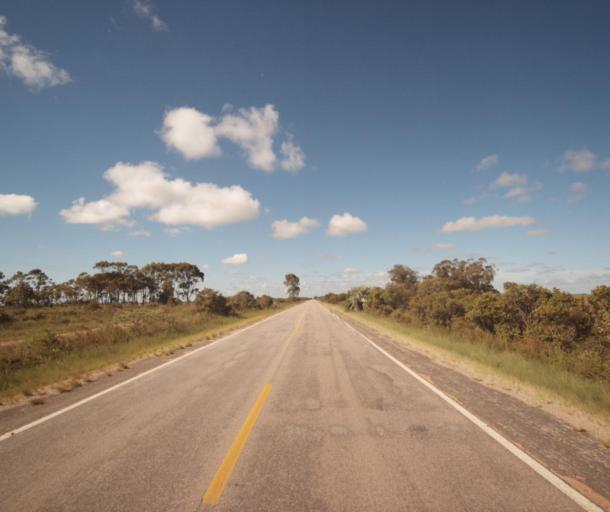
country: BR
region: Rio Grande do Sul
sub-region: Santa Vitoria Do Palmar
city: Santa Vitoria do Palmar
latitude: -33.3823
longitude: -53.1994
